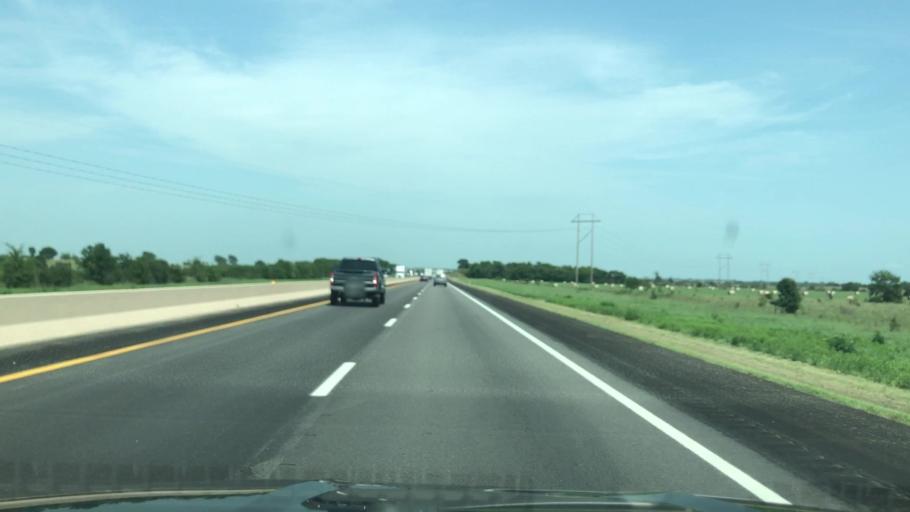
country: US
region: Oklahoma
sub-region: Ottawa County
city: Afton
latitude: 36.6735
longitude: -95.0603
